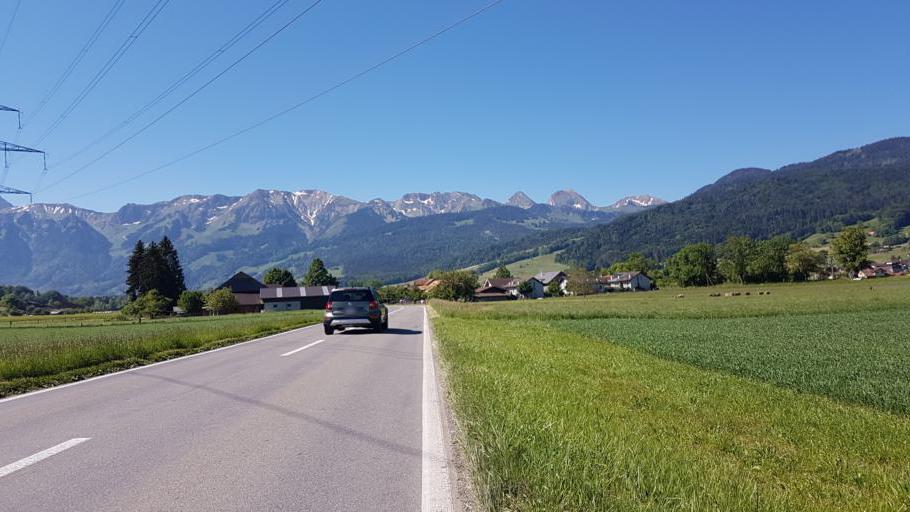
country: CH
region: Bern
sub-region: Thun District
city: Wattenwil
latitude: 46.7741
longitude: 7.5157
